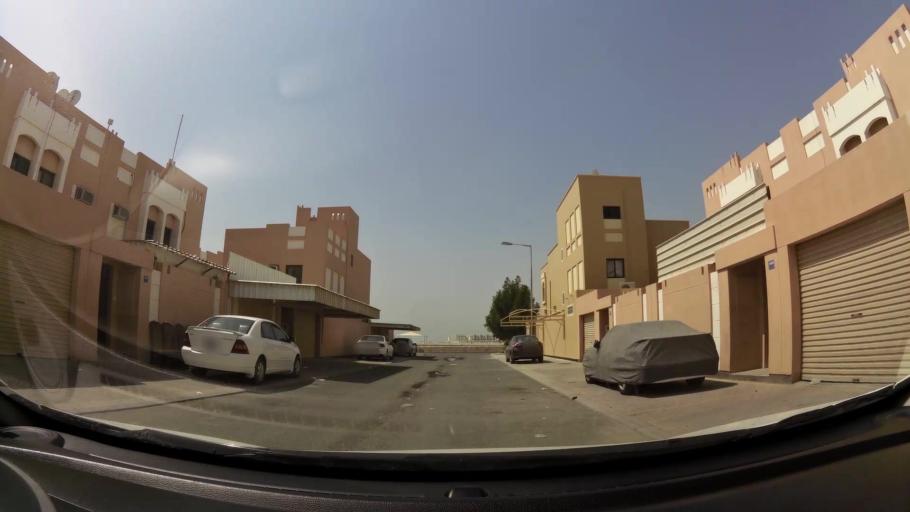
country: BH
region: Manama
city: Jidd Hafs
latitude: 26.2159
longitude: 50.4458
